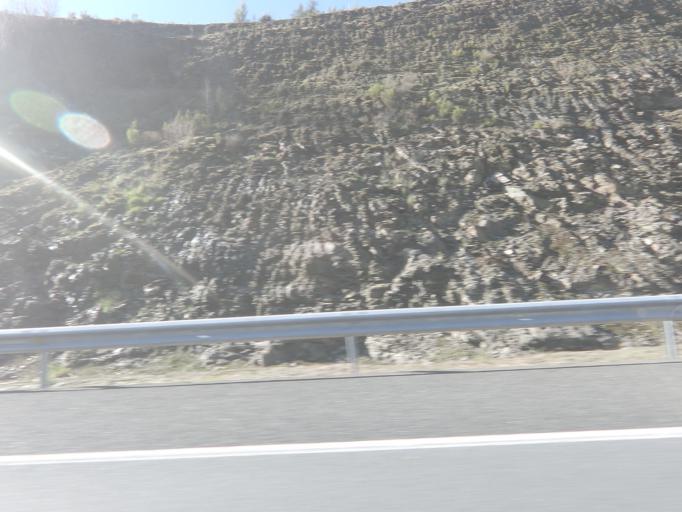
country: ES
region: Galicia
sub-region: Provincia de Pontevedra
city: Dozon
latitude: 42.5898
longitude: -8.0826
